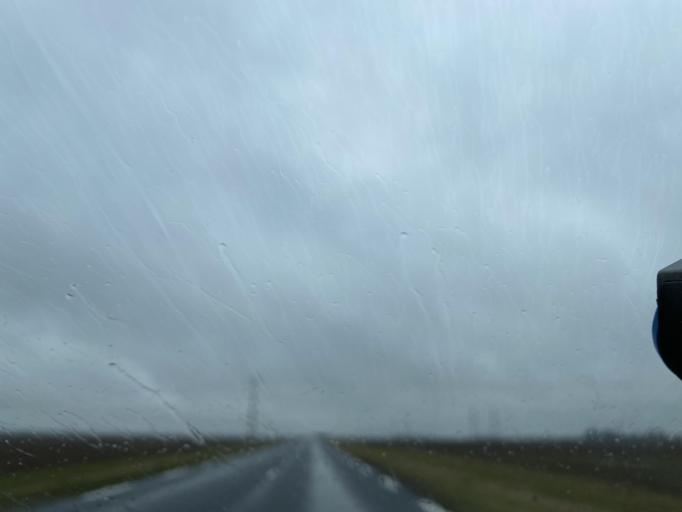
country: FR
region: Centre
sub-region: Departement d'Eure-et-Loir
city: Janville
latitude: 48.1895
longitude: 1.8299
